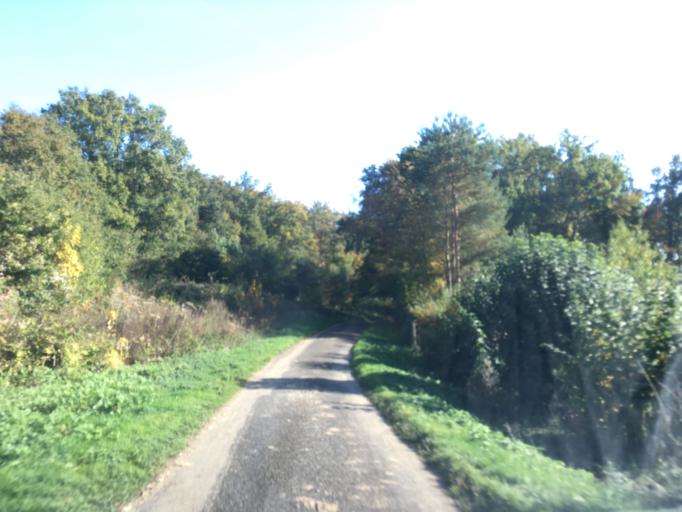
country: FR
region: Haute-Normandie
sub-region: Departement de l'Eure
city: Heudreville-sur-Eure
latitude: 49.1365
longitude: 1.2141
